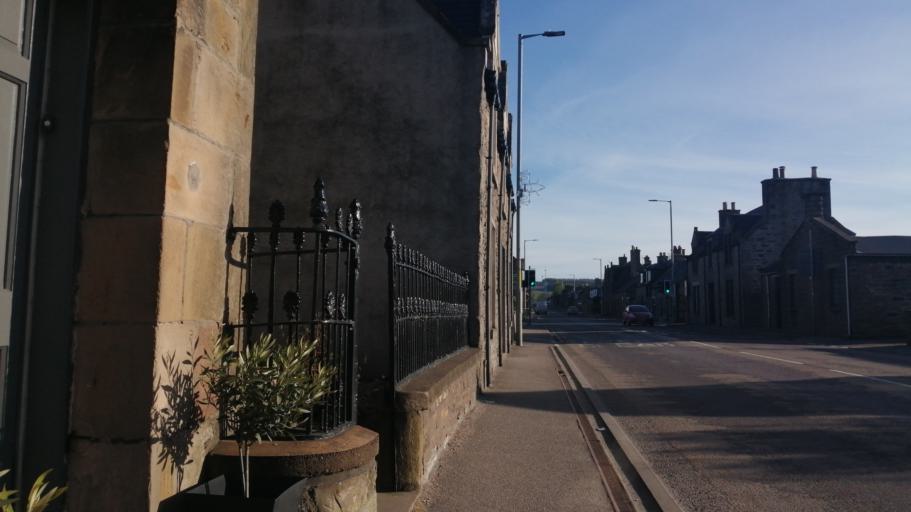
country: GB
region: Scotland
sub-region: Moray
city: Keith
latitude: 57.5424
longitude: -2.9479
